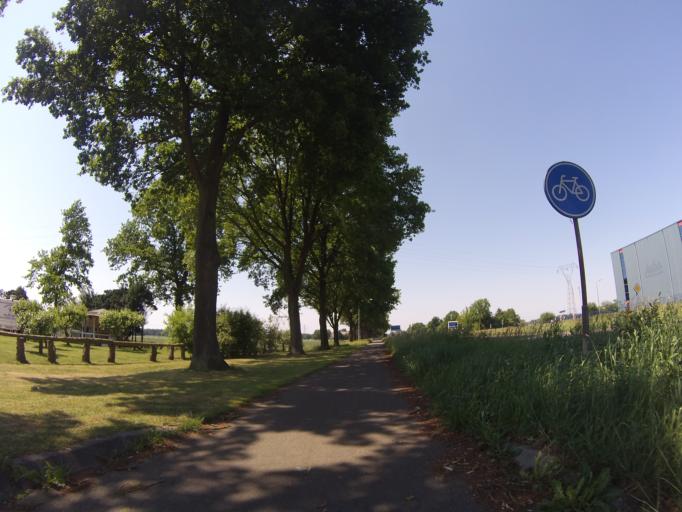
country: NL
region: Drenthe
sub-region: Gemeente Coevorden
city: Sleen
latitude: 52.7175
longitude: 6.8422
